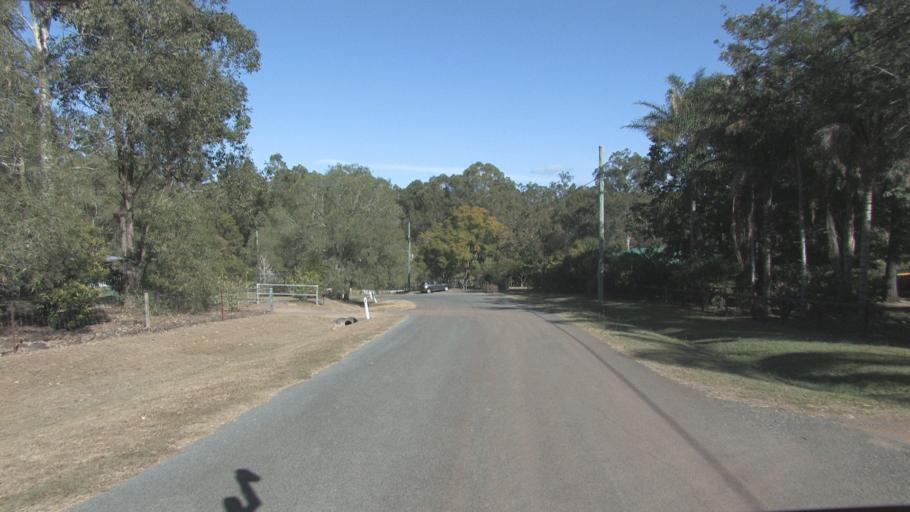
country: AU
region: Queensland
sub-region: Logan
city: Cedar Vale
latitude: -27.8573
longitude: 152.9869
